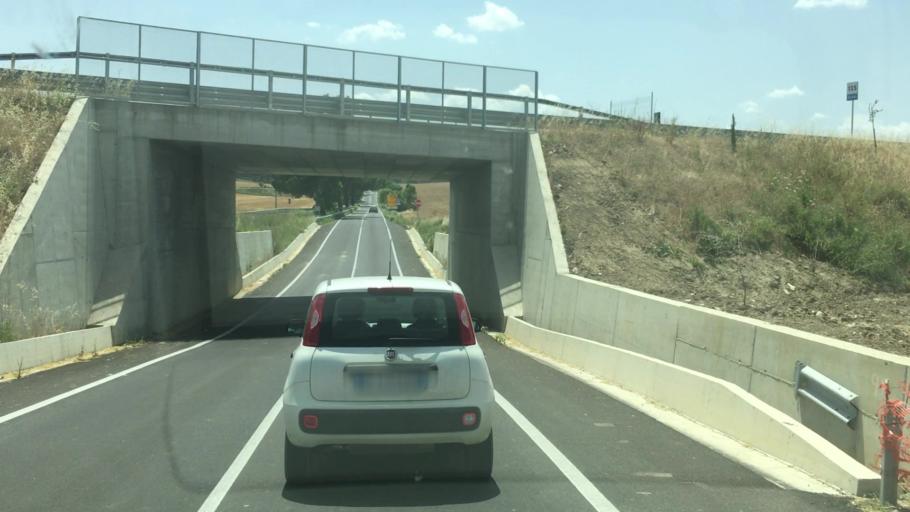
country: IT
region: Basilicate
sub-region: Provincia di Matera
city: La Martella
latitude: 40.6720
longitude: 16.4912
